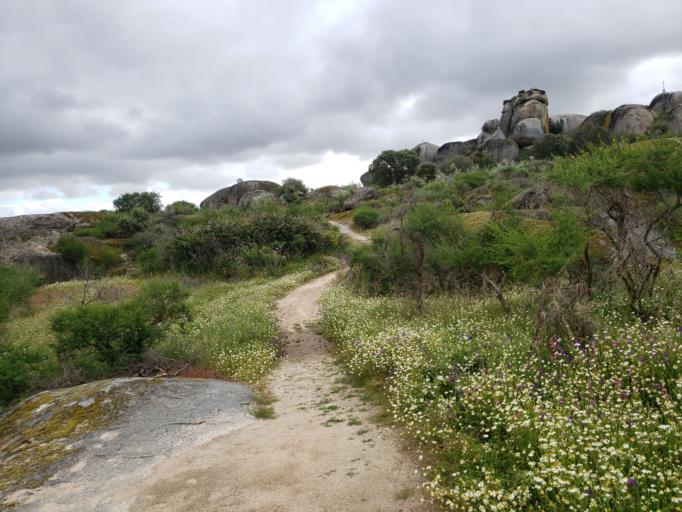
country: ES
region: Extremadura
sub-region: Provincia de Caceres
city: Malpartida de Caceres
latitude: 39.4218
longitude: -6.4983
